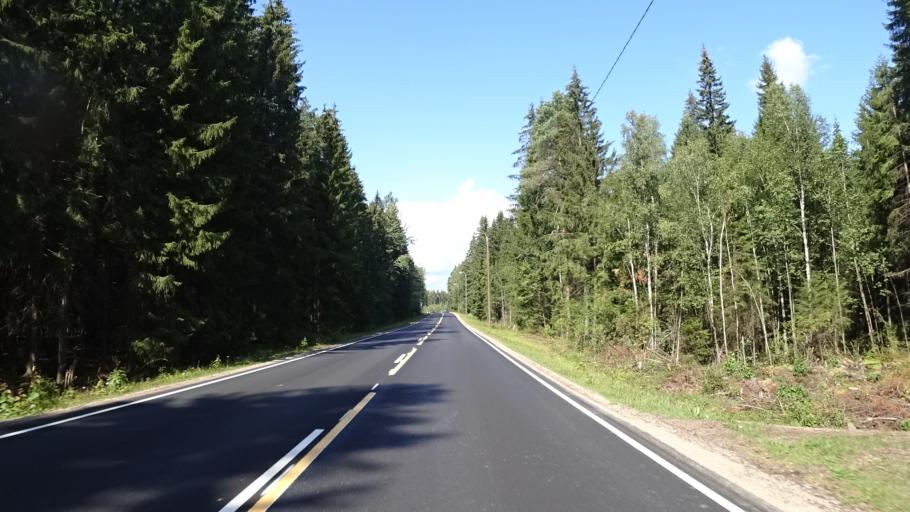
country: FI
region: Kymenlaakso
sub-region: Kotka-Hamina
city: Karhula
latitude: 60.5495
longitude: 26.9109
